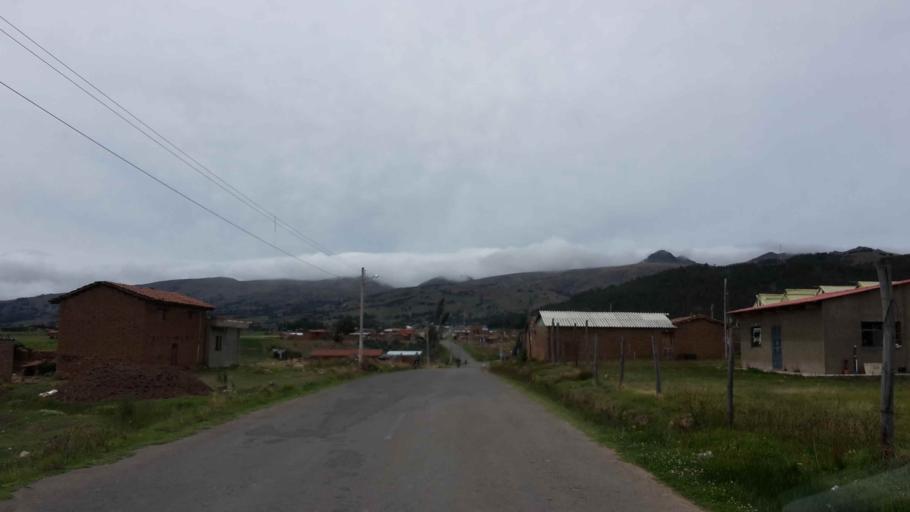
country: BO
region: Cochabamba
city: Arani
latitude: -17.4528
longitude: -65.7193
